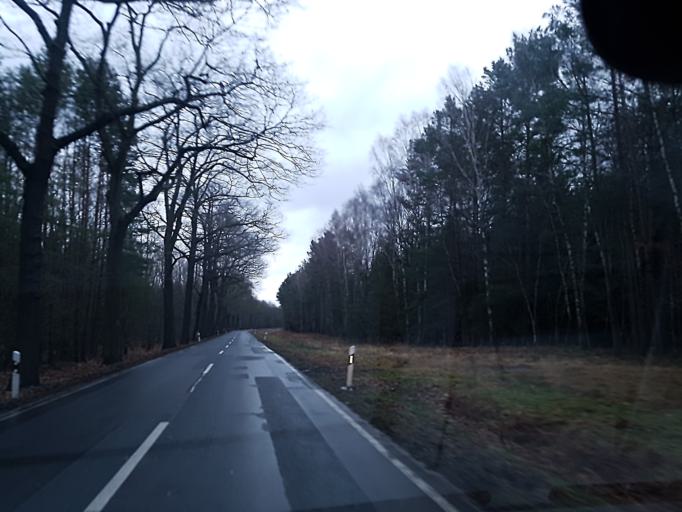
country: DE
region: Brandenburg
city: Hohenleipisch
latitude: 51.5248
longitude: 13.5796
